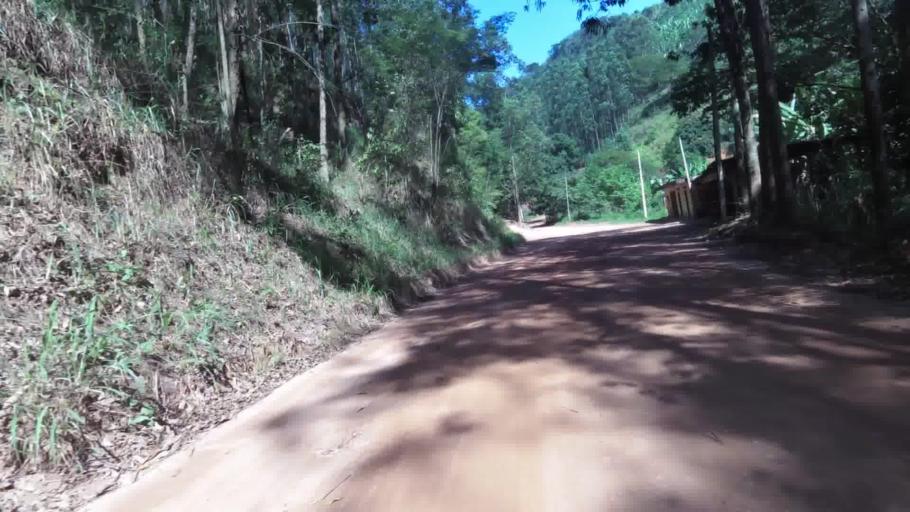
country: BR
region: Espirito Santo
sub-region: Alfredo Chaves
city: Alfredo Chaves
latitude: -20.6458
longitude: -40.7926
